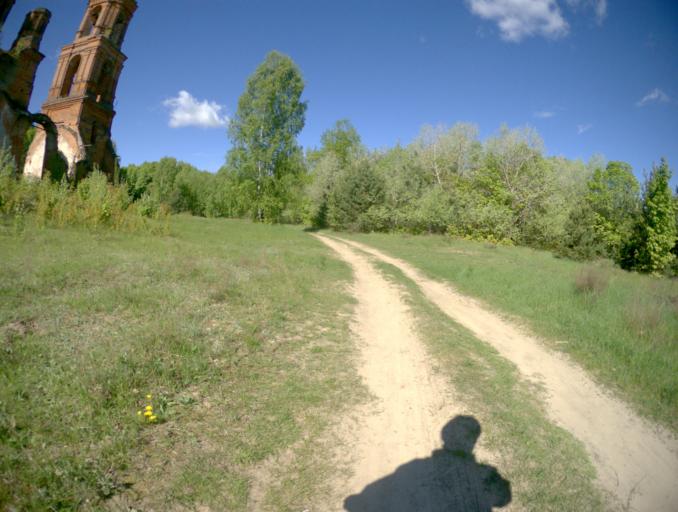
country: RU
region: Rjazan
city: Spas-Klepiki
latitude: 55.2537
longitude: 40.1137
